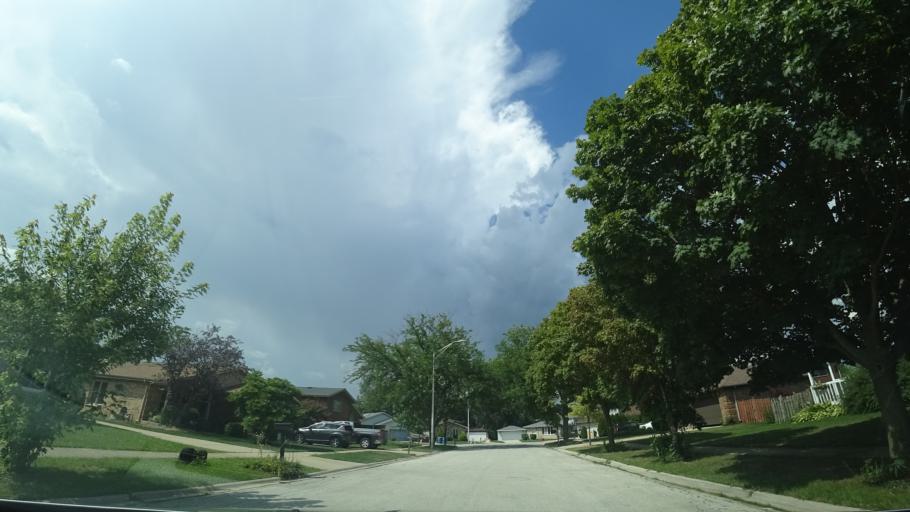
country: US
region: Illinois
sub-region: Cook County
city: Merrionette Park
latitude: 41.6735
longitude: -87.7166
